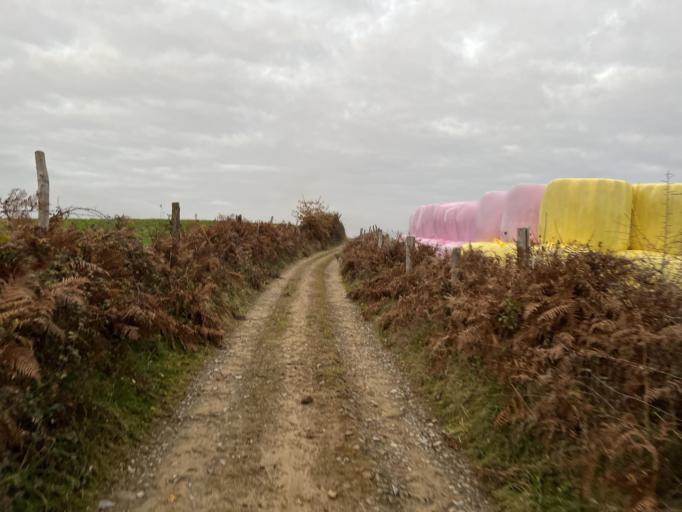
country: FR
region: Limousin
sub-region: Departement de la Correze
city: Sainte-Fortunade
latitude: 45.2204
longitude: 1.7791
